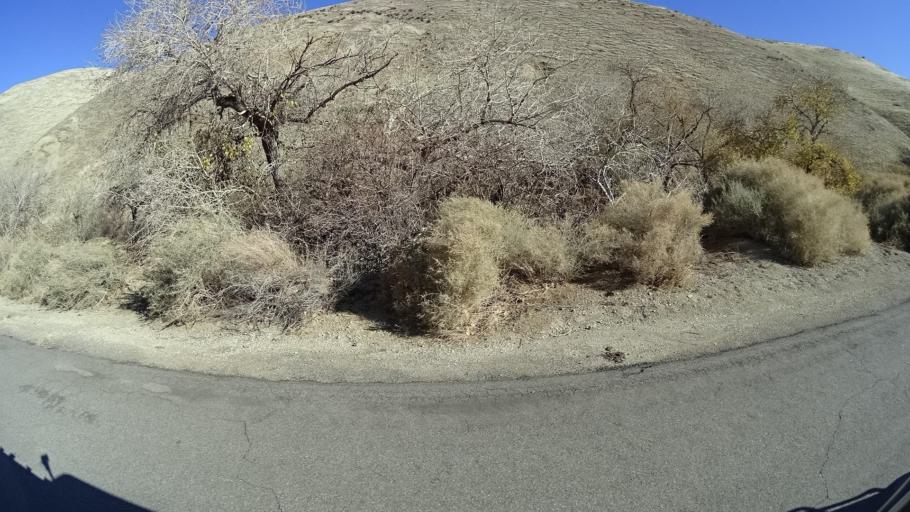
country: US
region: California
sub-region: Kern County
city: Maricopa
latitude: 34.9674
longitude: -119.4133
